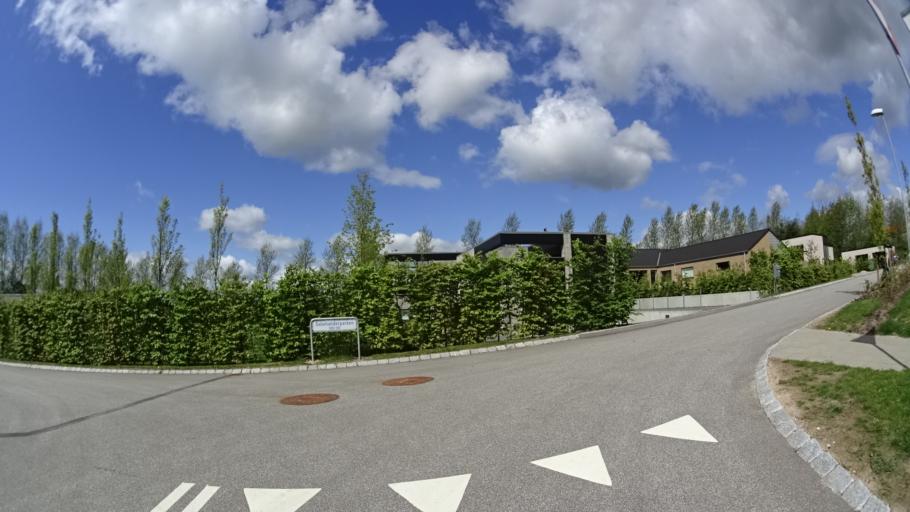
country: DK
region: Central Jutland
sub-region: Arhus Kommune
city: Stavtrup
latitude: 56.1281
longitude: 10.1003
